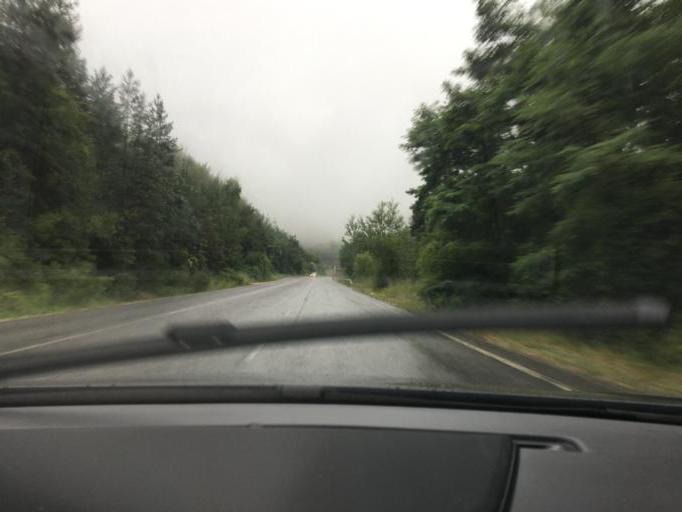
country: MK
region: Kriva Palanka
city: Kriva Palanka
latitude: 42.2191
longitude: 22.4724
